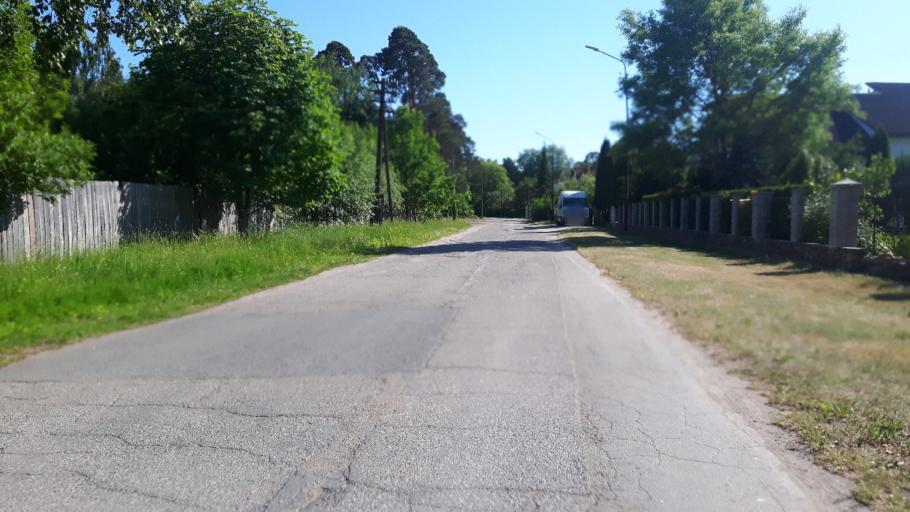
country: LV
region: Salacgrivas
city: Salacgriva
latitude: 57.7483
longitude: 24.3541
